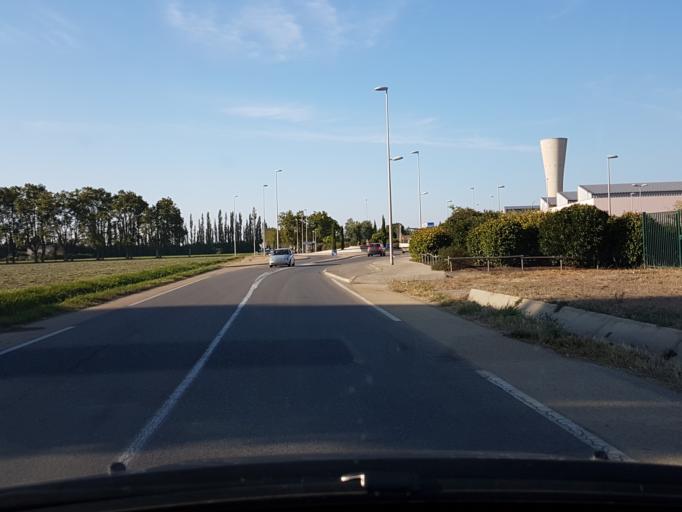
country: FR
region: Provence-Alpes-Cote d'Azur
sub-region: Departement des Bouches-du-Rhone
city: Molleges
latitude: 43.8204
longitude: 4.9479
